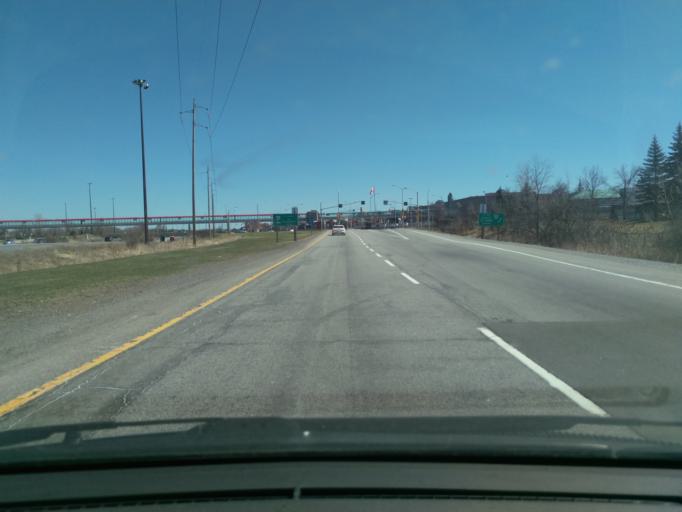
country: CA
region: Quebec
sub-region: Outaouais
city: Gatineau
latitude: 45.4777
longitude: -75.5226
